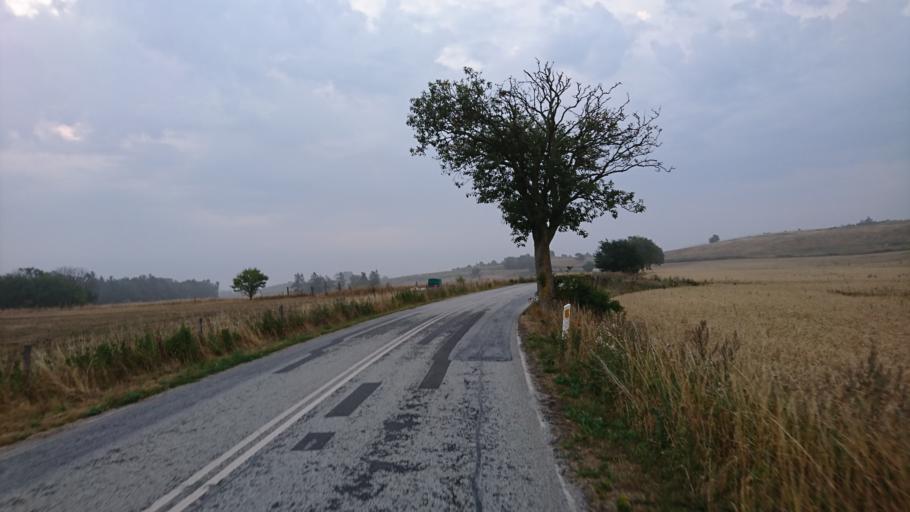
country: DK
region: Capital Region
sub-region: Egedal Kommune
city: Smorumnedre
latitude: 55.7590
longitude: 12.3008
